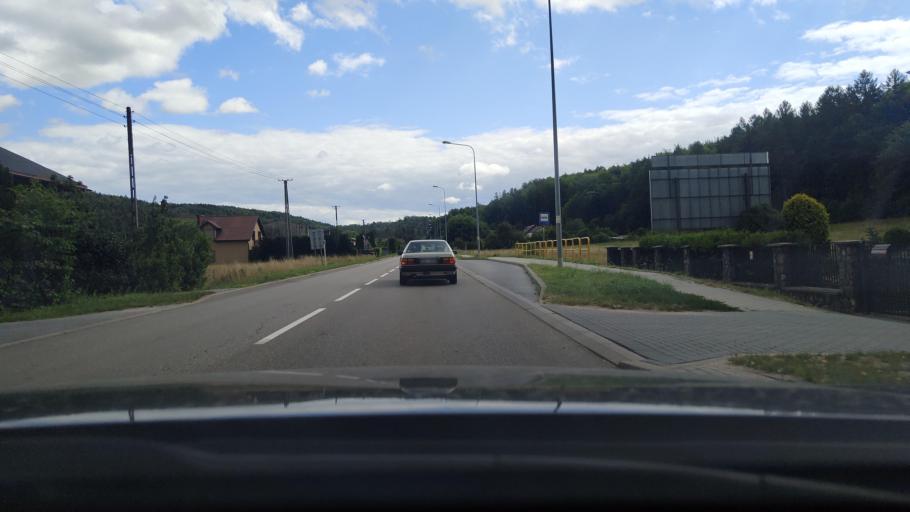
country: PL
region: Pomeranian Voivodeship
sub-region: Powiat wejherowski
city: Wejherowo
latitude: 54.5899
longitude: 18.2433
